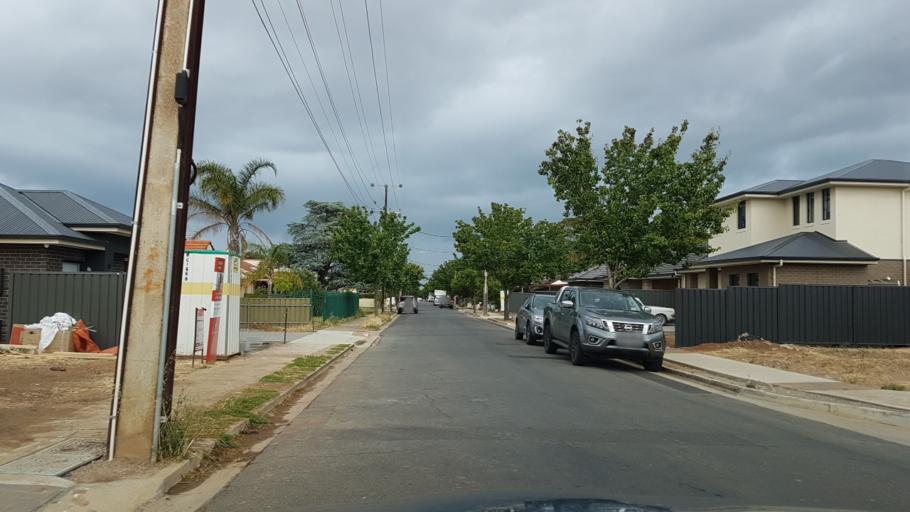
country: AU
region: South Australia
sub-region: City of West Torrens
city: Plympton
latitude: -34.9564
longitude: 138.5565
